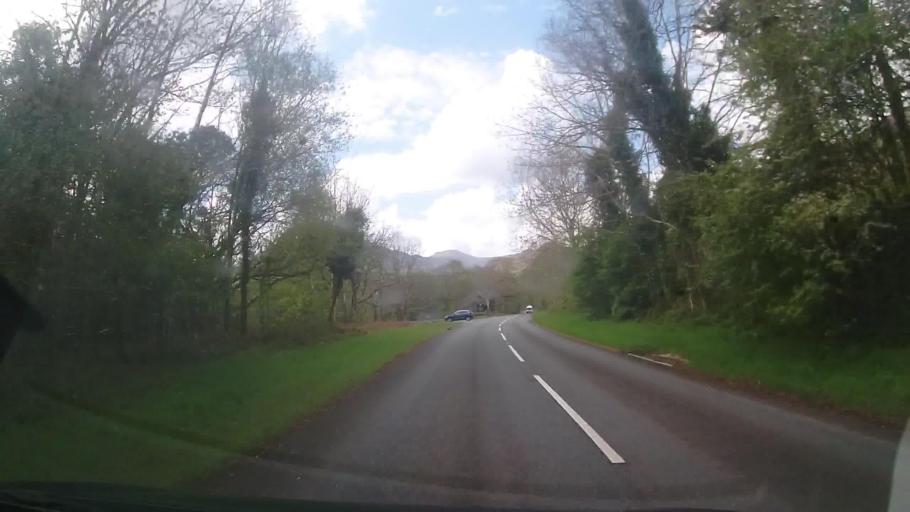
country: GB
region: Wales
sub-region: Gwynedd
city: Penrhyndeudraeth
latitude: 53.0204
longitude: -4.0803
